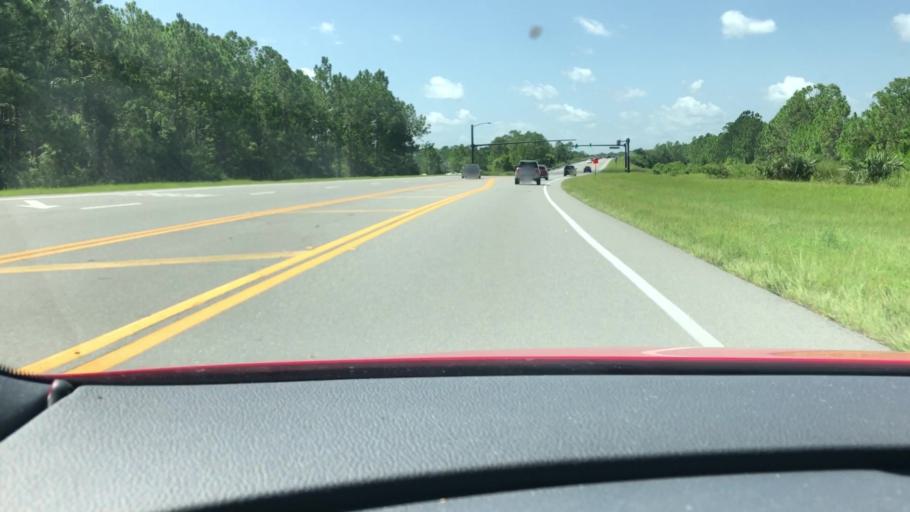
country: US
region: Florida
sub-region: Volusia County
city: Port Orange
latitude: 29.1276
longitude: -81.0466
